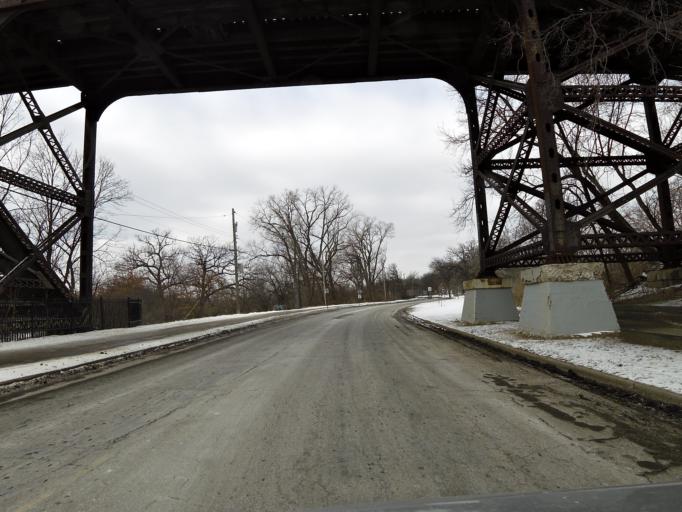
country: US
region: Minnesota
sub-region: Ramsey County
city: Lauderdale
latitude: 44.9568
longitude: -93.2110
